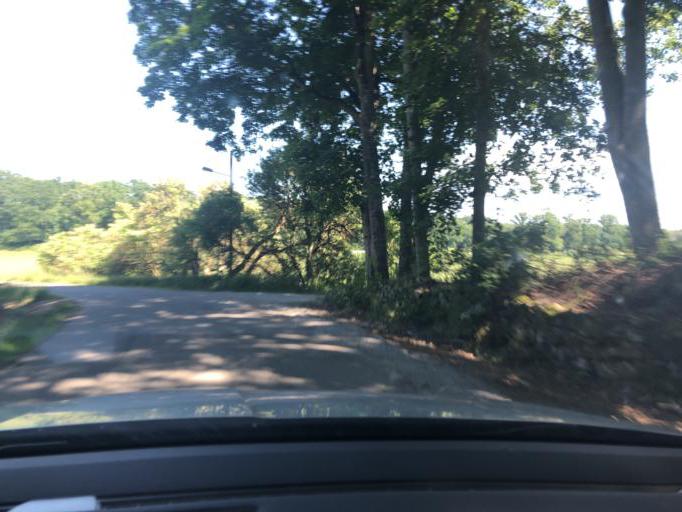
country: SE
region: Blekinge
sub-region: Karlshamns Kommun
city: Morrum
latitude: 56.1727
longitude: 14.7095
